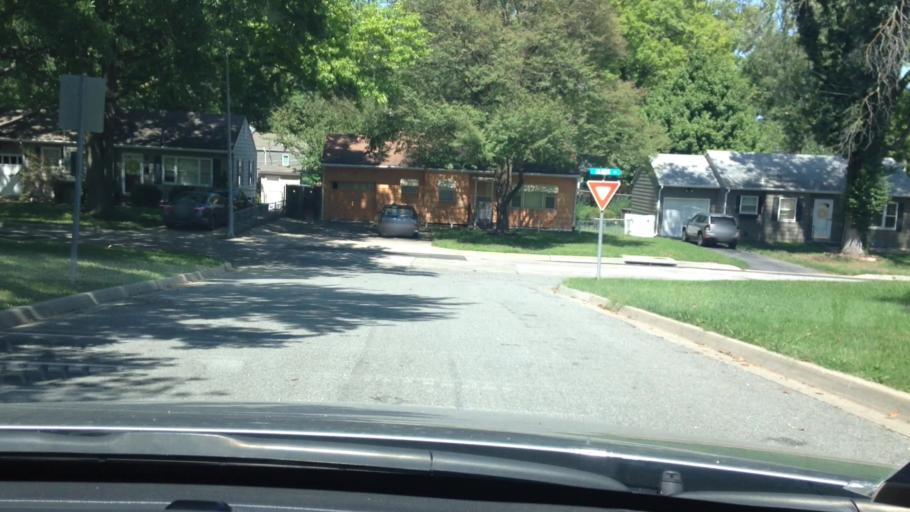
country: US
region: Kansas
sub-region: Johnson County
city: Roeland Park
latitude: 39.0325
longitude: -94.6437
